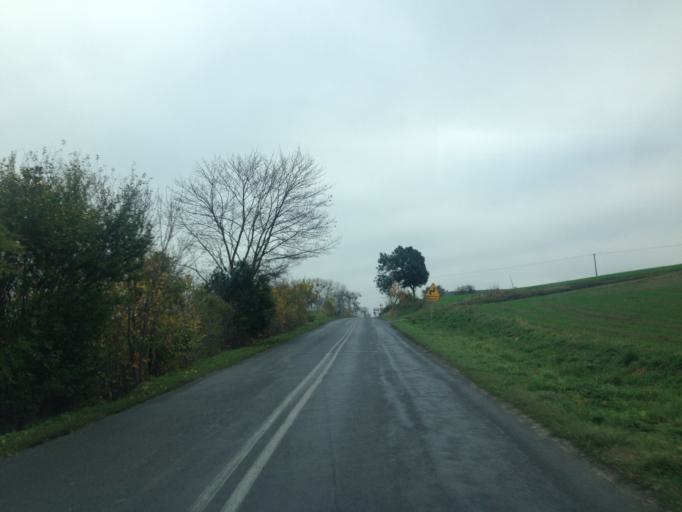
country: PL
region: Kujawsko-Pomorskie
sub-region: Powiat brodnicki
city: Jablonowo Pomorskie
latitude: 53.3738
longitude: 19.1757
